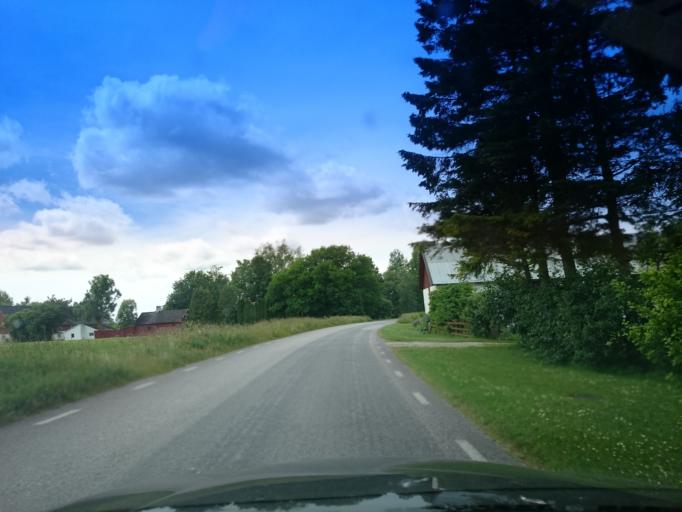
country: SE
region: Gotland
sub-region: Gotland
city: Hemse
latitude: 57.2558
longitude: 18.6133
